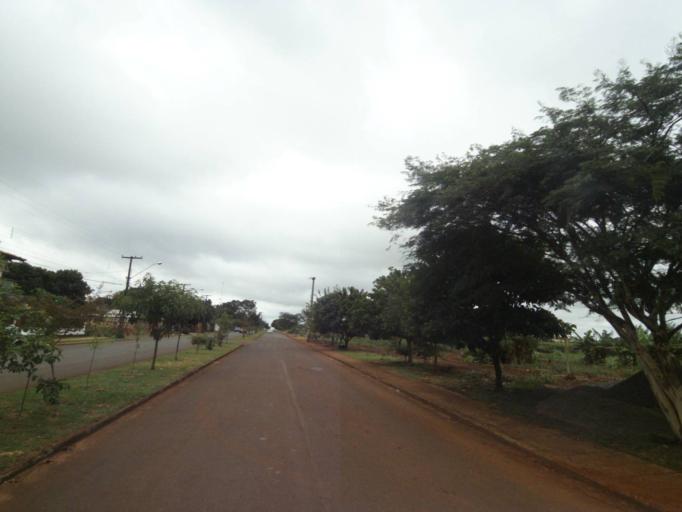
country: BR
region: Parana
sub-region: Campo Mourao
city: Campo Mourao
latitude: -24.0131
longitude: -52.3557
